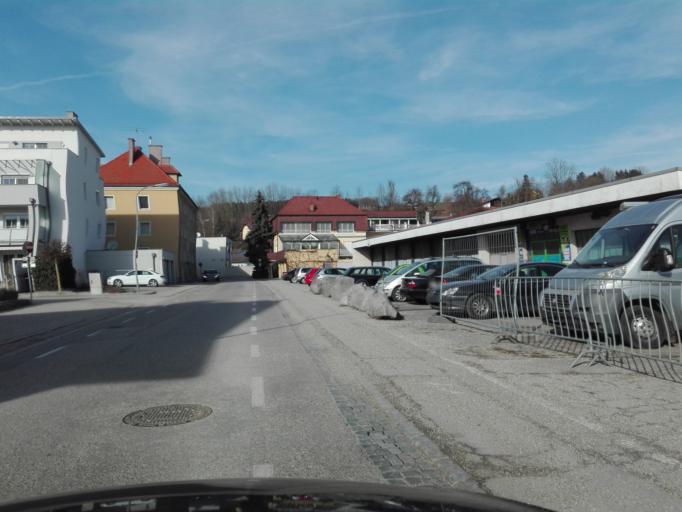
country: AT
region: Upper Austria
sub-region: Politischer Bezirk Perg
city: Perg
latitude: 48.2481
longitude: 14.6403
